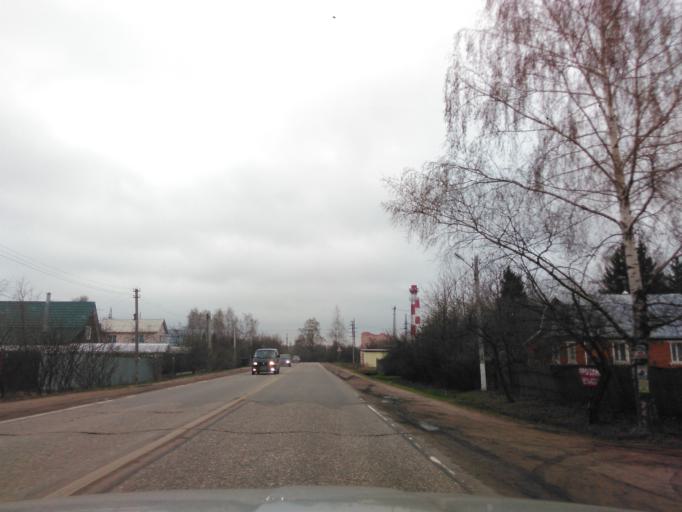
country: RU
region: Moskovskaya
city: Nakhabino
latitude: 55.8316
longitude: 37.1527
